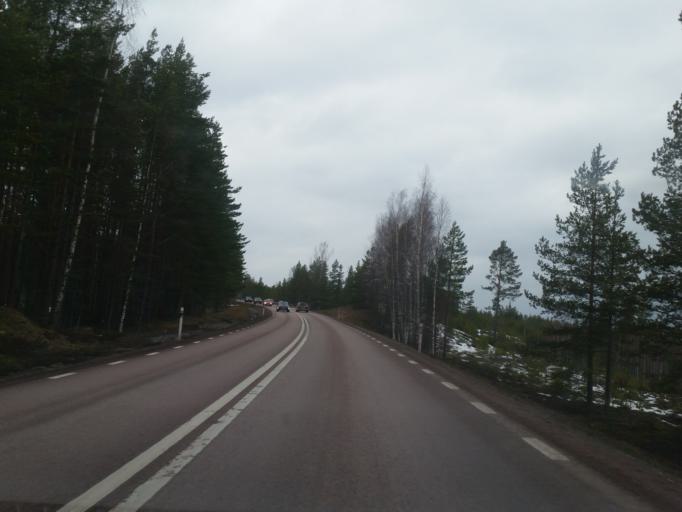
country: SE
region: Dalarna
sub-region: Mora Kommun
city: Mora
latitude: 61.0475
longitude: 14.4924
